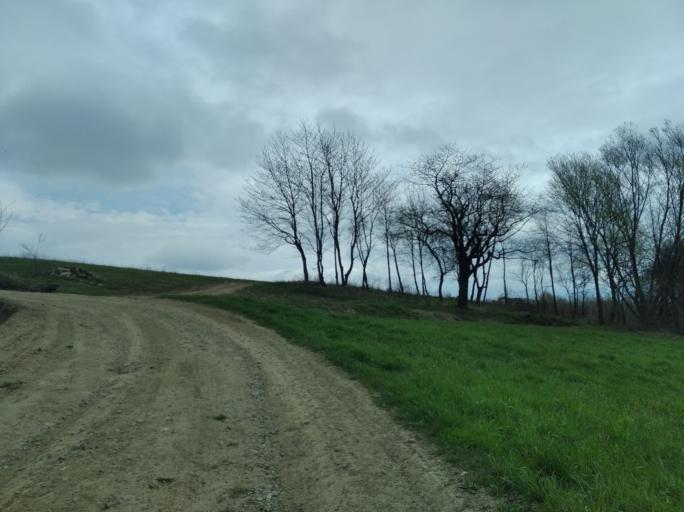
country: PL
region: Subcarpathian Voivodeship
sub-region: Powiat strzyzowski
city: Jawornik
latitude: 49.8177
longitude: 21.8974
